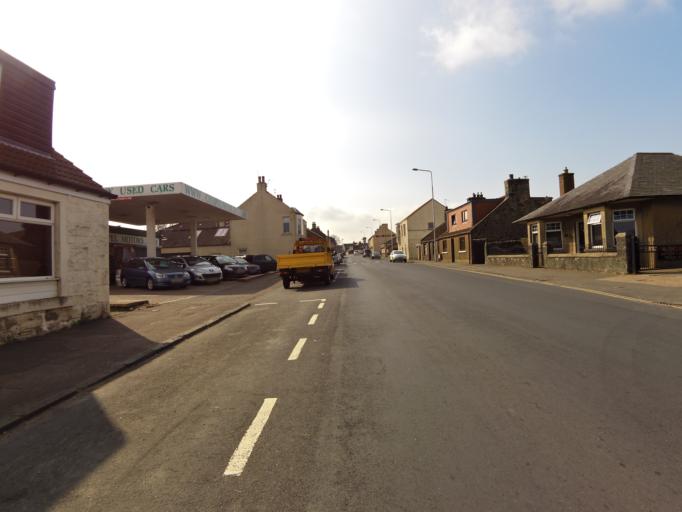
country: GB
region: Scotland
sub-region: Fife
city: Thornton
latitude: 56.1680
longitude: -3.1461
